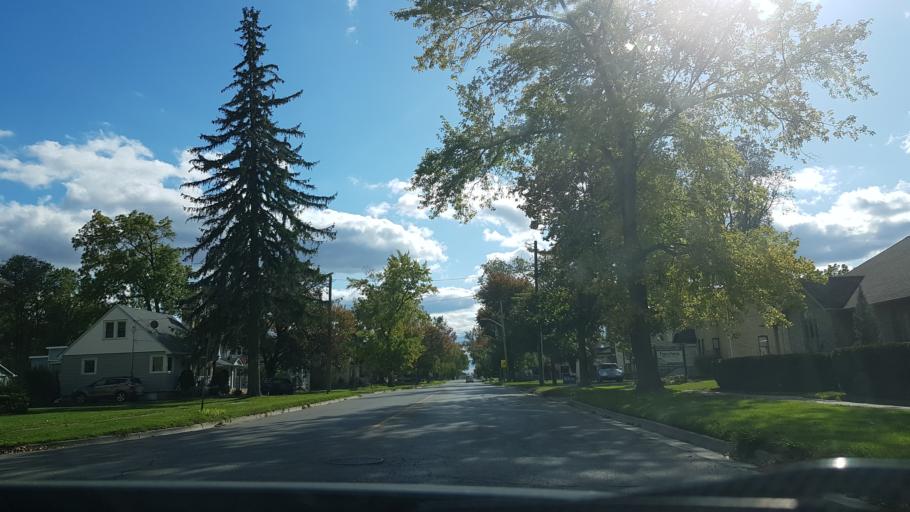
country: CA
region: Ontario
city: South Huron
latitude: 43.1591
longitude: -81.6852
